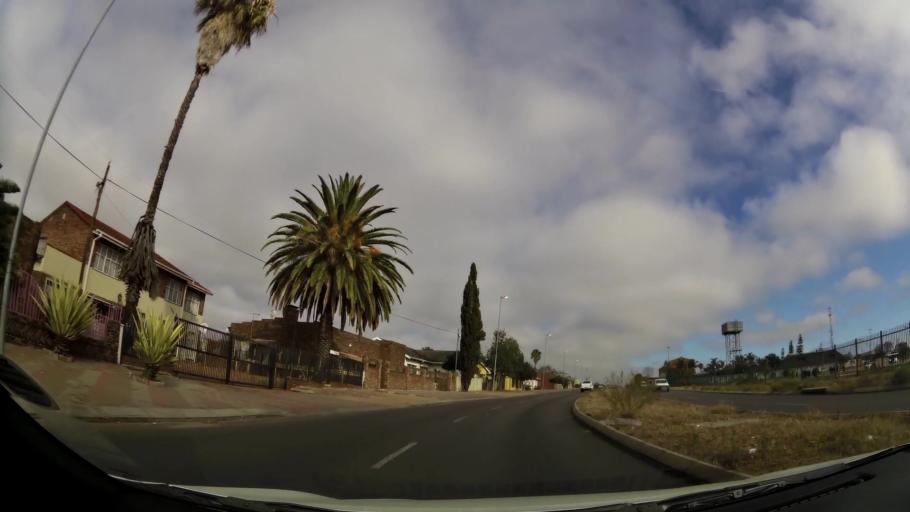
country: ZA
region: Limpopo
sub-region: Capricorn District Municipality
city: Polokwane
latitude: -23.8550
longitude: 29.3846
